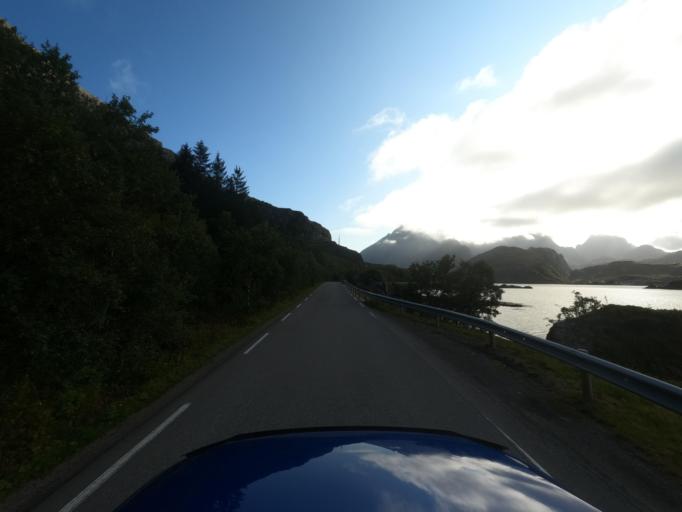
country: NO
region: Nordland
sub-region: Flakstad
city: Ramberg
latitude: 68.0175
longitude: 13.2010
